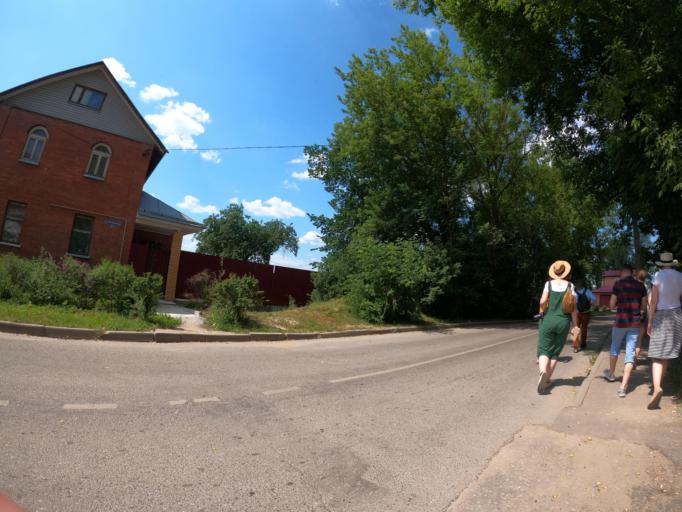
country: RU
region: Moskovskaya
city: Serpukhov
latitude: 54.9161
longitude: 37.4097
